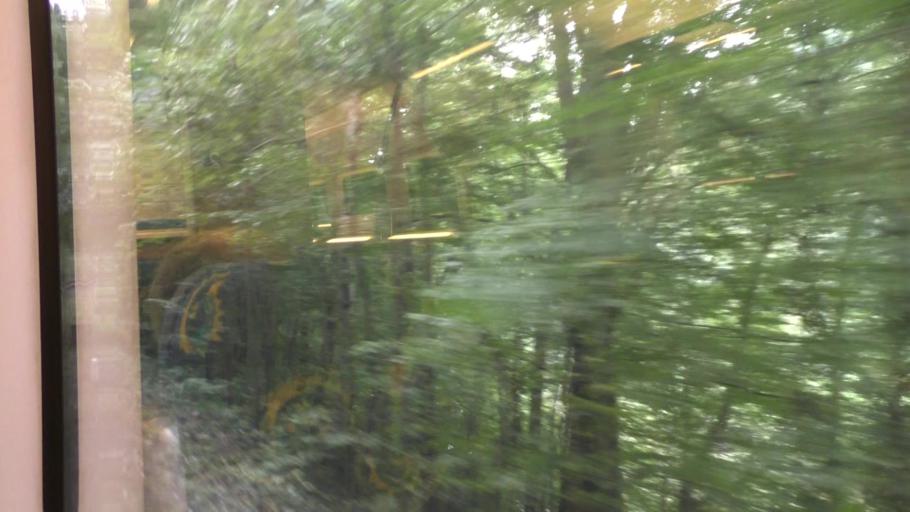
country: DE
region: Saxony
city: Schlegel
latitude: 50.9679
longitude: 14.9048
